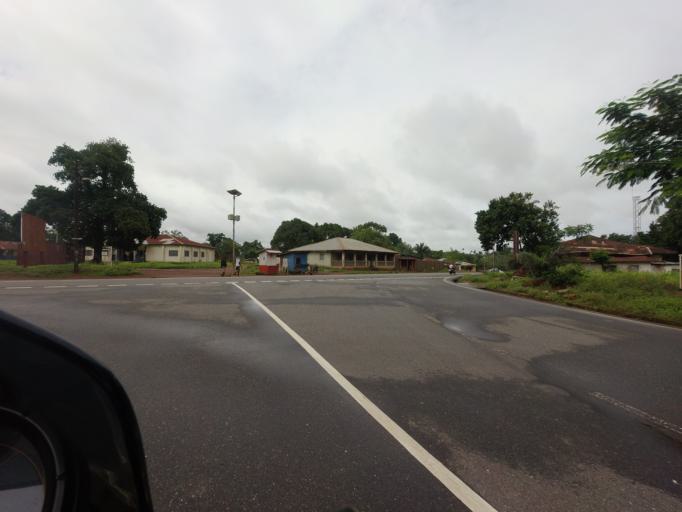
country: SL
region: Northern Province
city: Kambia
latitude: 9.1223
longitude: -12.9182
